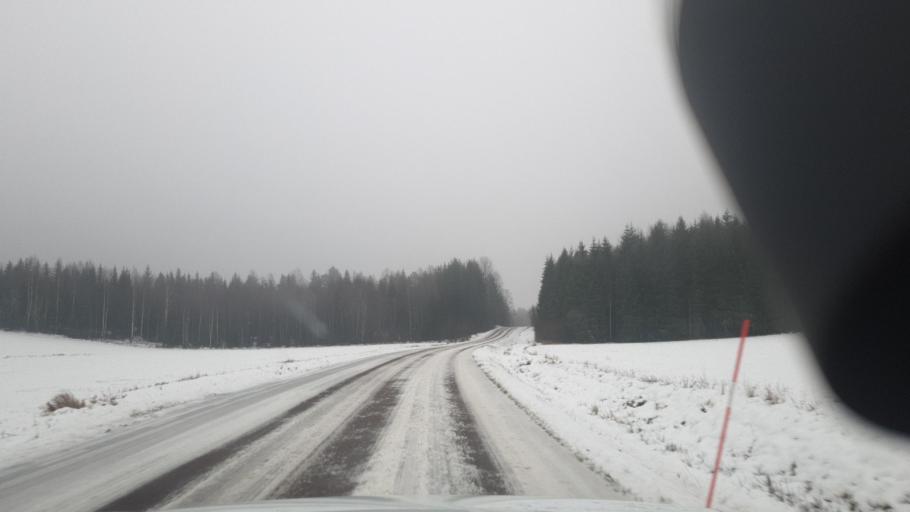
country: SE
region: Vaermland
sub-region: Karlstads Kommun
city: Edsvalla
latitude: 59.5224
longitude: 13.1123
